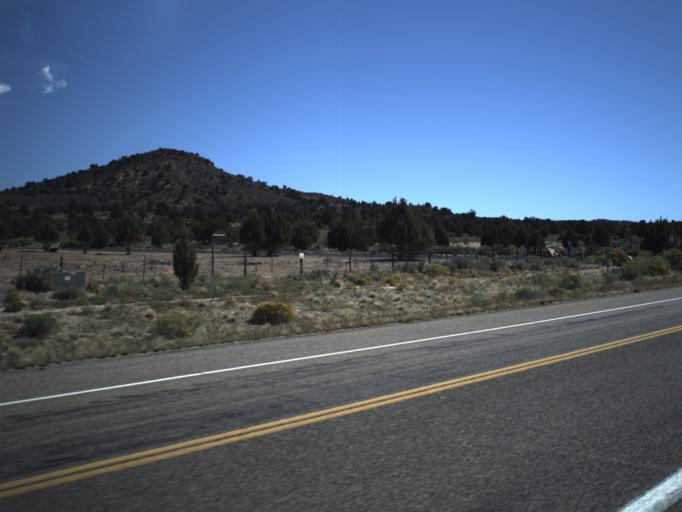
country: US
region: Utah
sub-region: Washington County
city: Ivins
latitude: 37.3016
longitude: -113.6679
